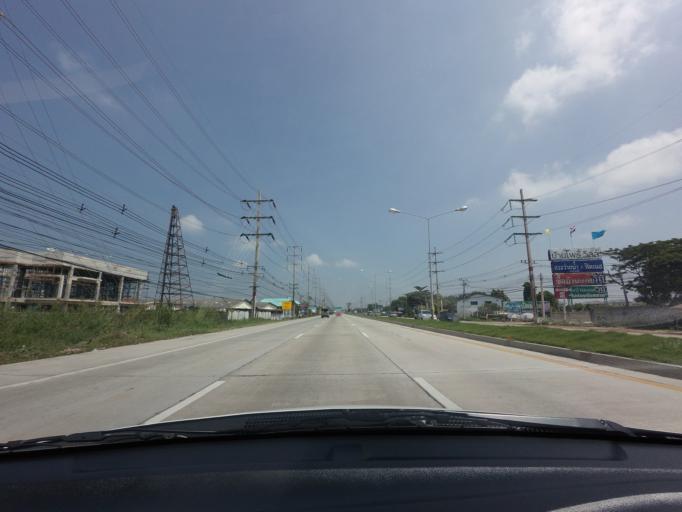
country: TH
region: Chachoengsao
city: Ban Pho
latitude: 13.6261
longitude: 101.0339
